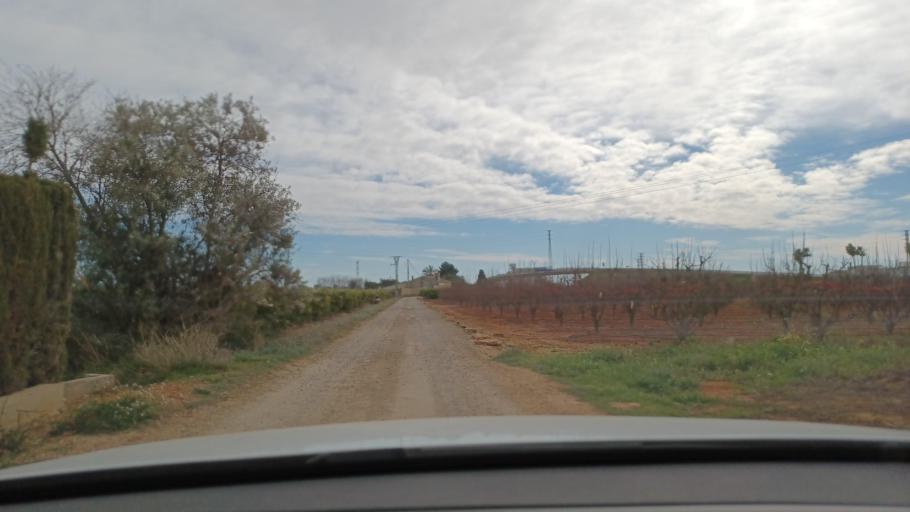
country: ES
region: Valencia
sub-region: Provincia de Valencia
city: Benifaio
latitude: 39.2908
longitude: -0.4417
